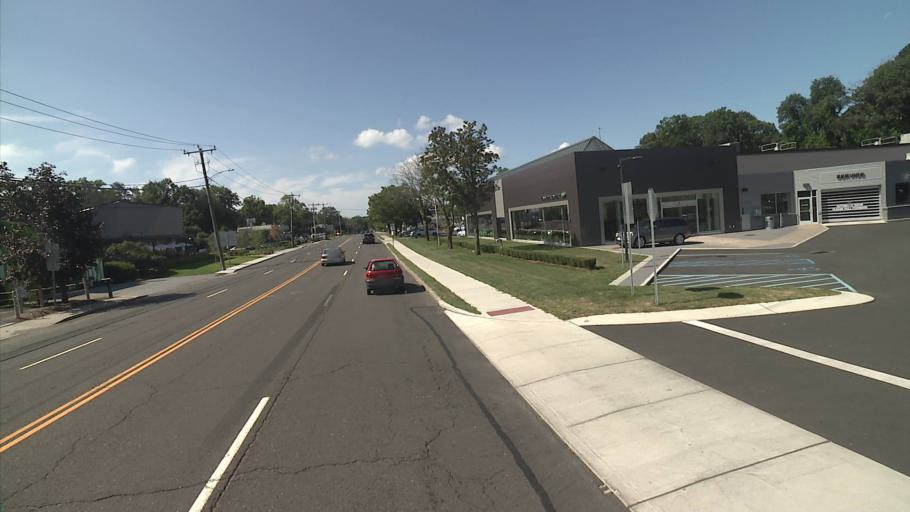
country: US
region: Connecticut
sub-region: Fairfield County
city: Darien
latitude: 41.0708
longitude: -73.4763
